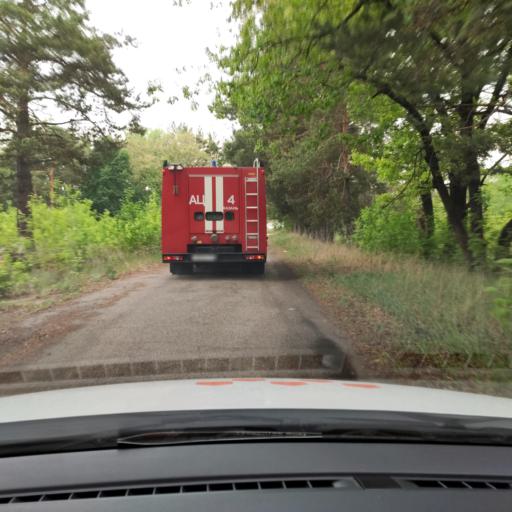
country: RU
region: Tatarstan
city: Staroye Arakchino
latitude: 55.8065
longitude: 48.9673
